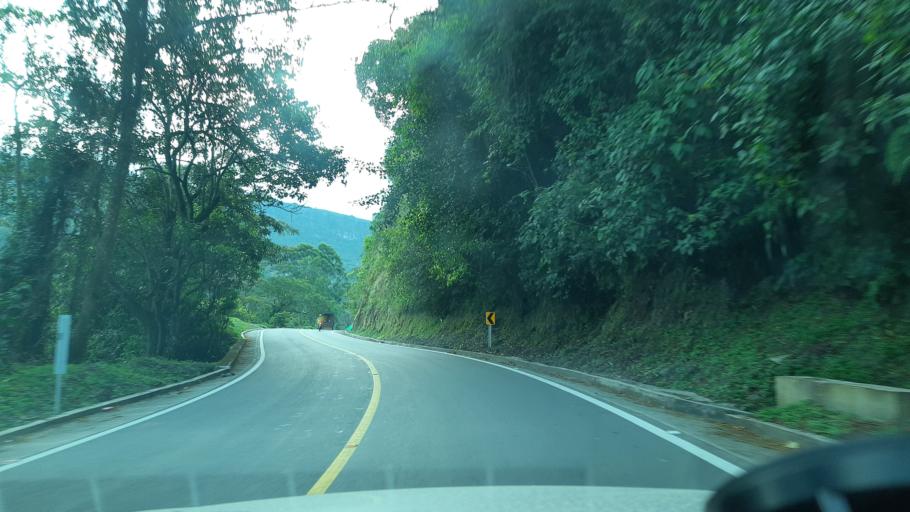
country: CO
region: Boyaca
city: Somondoco
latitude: 4.9805
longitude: -73.3414
